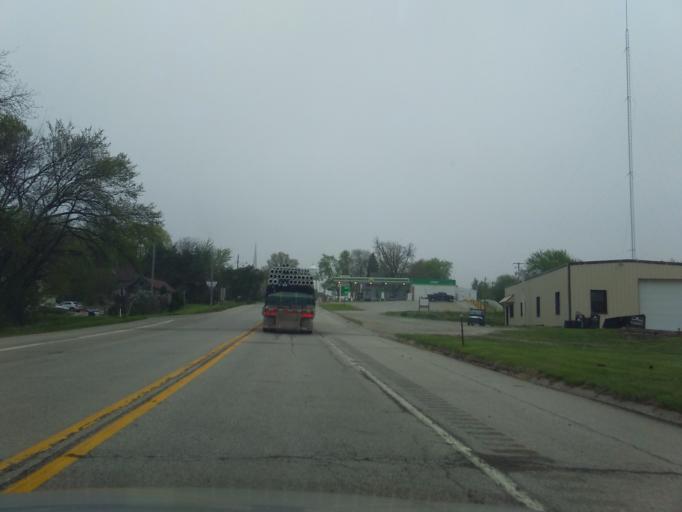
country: US
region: Nebraska
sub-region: Burt County
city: Oakland
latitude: 41.8318
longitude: -96.4631
